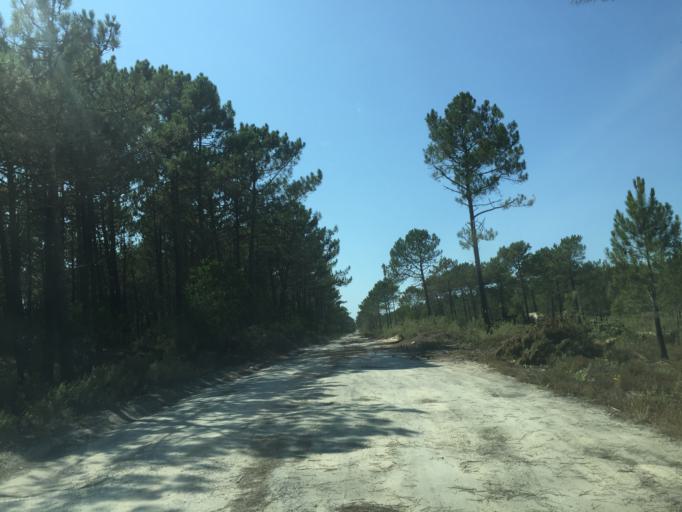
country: PT
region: Coimbra
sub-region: Figueira da Foz
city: Tavarede
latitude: 40.2585
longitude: -8.8431
